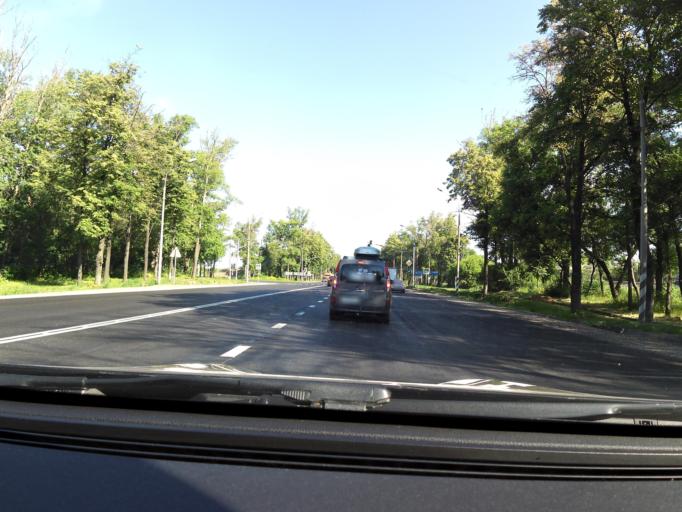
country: RU
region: Tverskaya
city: Zavidovo
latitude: 56.5776
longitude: 36.4966
